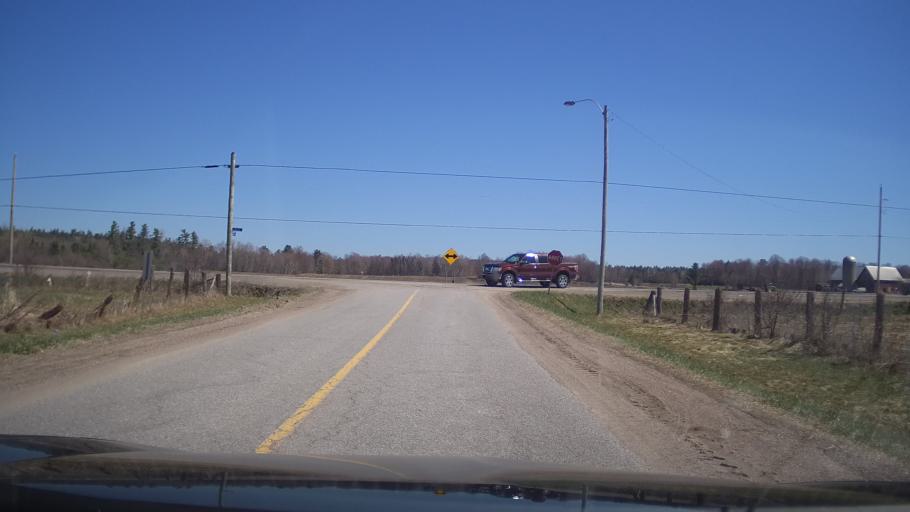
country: CA
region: Quebec
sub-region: Outaouais
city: Shawville
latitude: 45.5508
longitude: -76.3843
